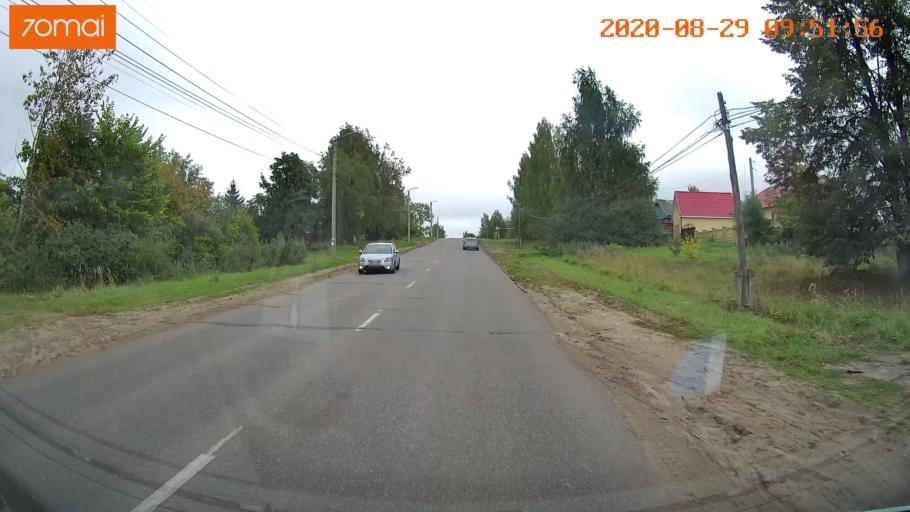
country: RU
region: Ivanovo
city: Kineshma
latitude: 57.4265
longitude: 42.2036
